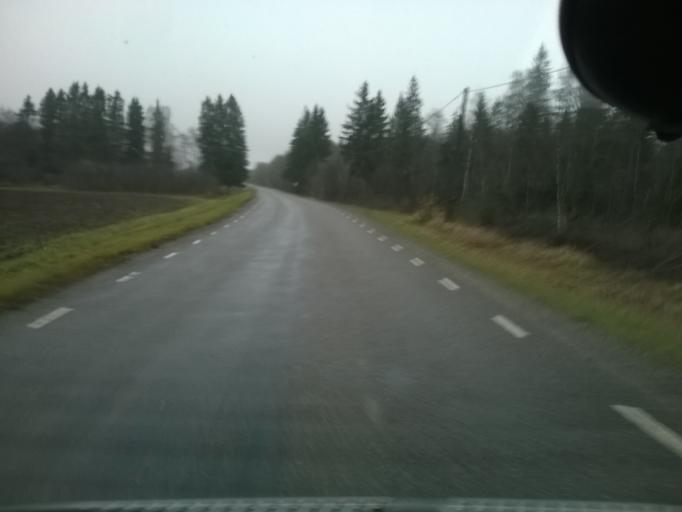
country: EE
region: Raplamaa
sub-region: Kohila vald
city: Kohila
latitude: 59.2018
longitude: 24.6689
